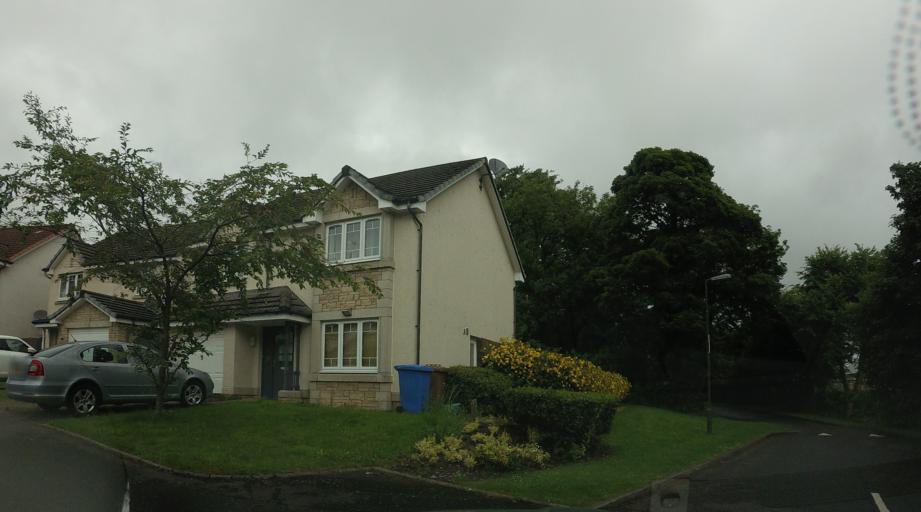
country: GB
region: Scotland
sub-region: West Lothian
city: Broxburn
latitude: 55.9273
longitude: -3.5005
